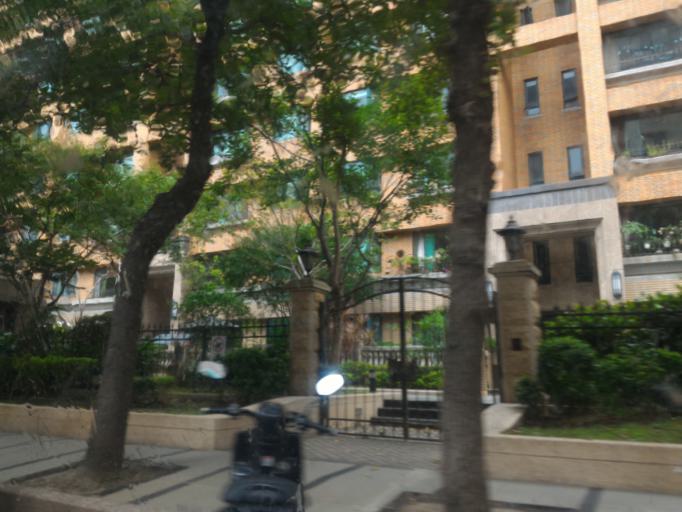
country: TW
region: Taipei
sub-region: Taipei
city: Banqiao
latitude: 25.0875
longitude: 121.4587
